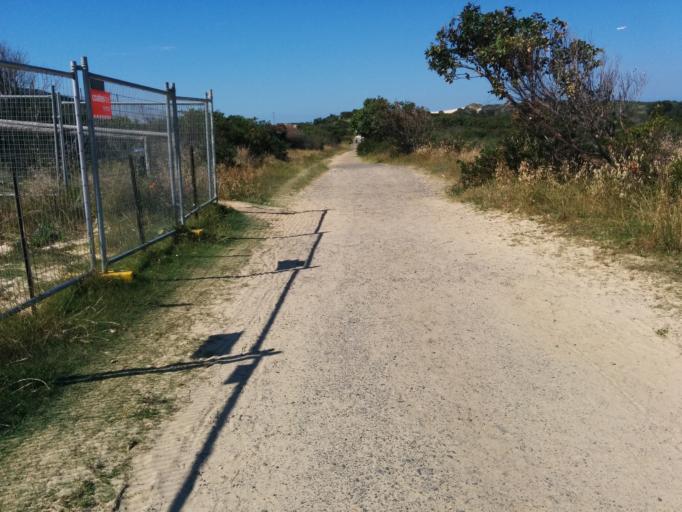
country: AU
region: New South Wales
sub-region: Sutherland Shire
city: Cronulla
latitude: -34.0373
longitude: 151.1651
